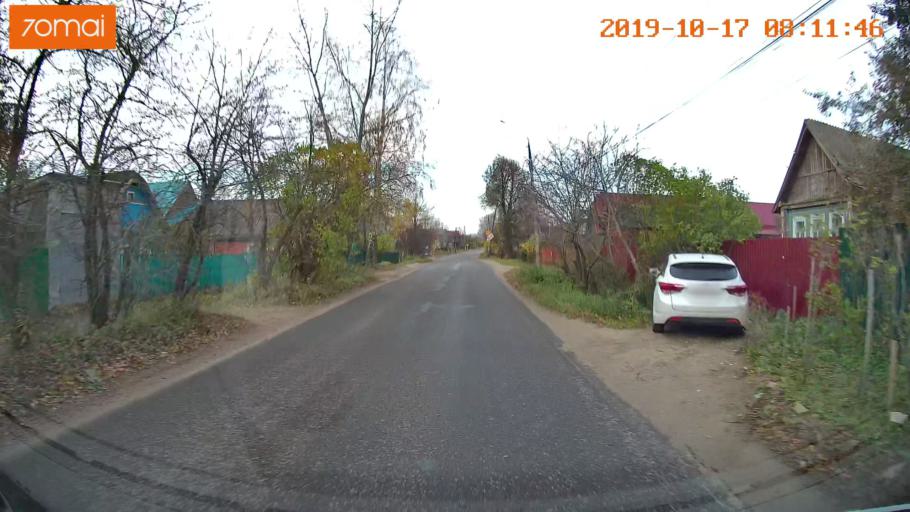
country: RU
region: Vladimir
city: Kol'chugino
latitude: 56.3014
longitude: 39.3654
